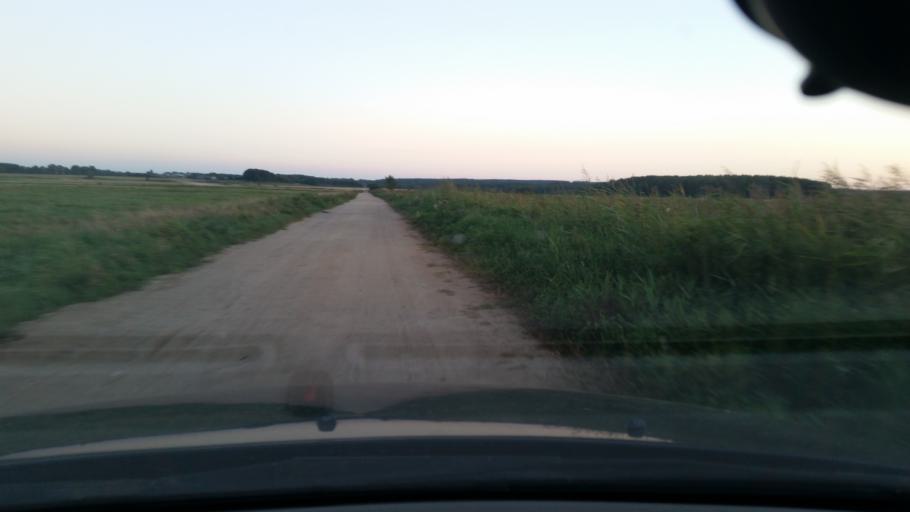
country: PL
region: Pomeranian Voivodeship
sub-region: Powiat wejherowski
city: Choczewo
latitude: 54.7871
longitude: 17.7952
